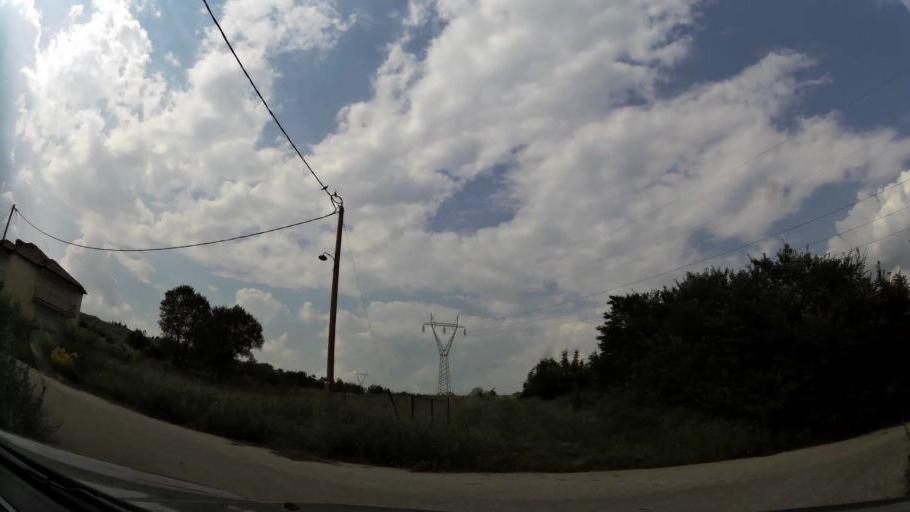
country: GR
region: West Macedonia
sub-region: Nomos Kozanis
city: Koila
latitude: 40.3486
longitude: 21.8221
